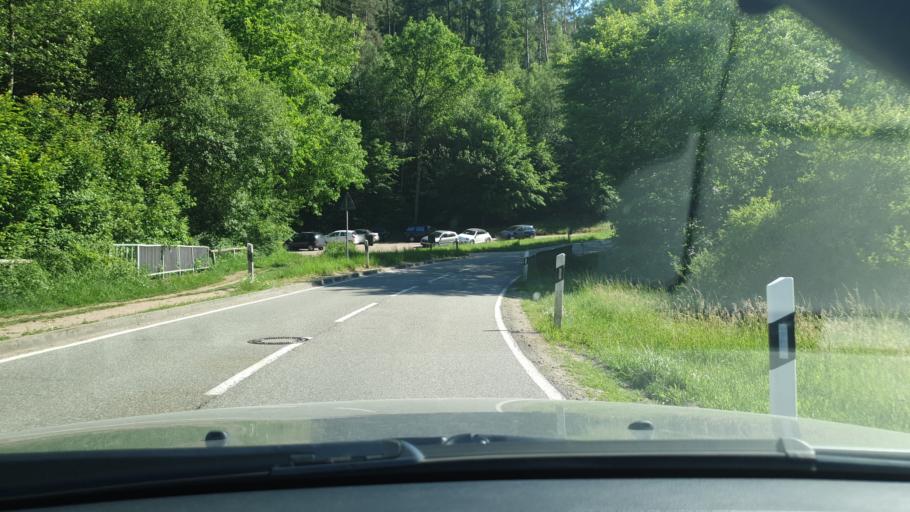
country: DE
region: Rheinland-Pfalz
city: Kaiserslautern
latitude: 49.4687
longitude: 7.7872
